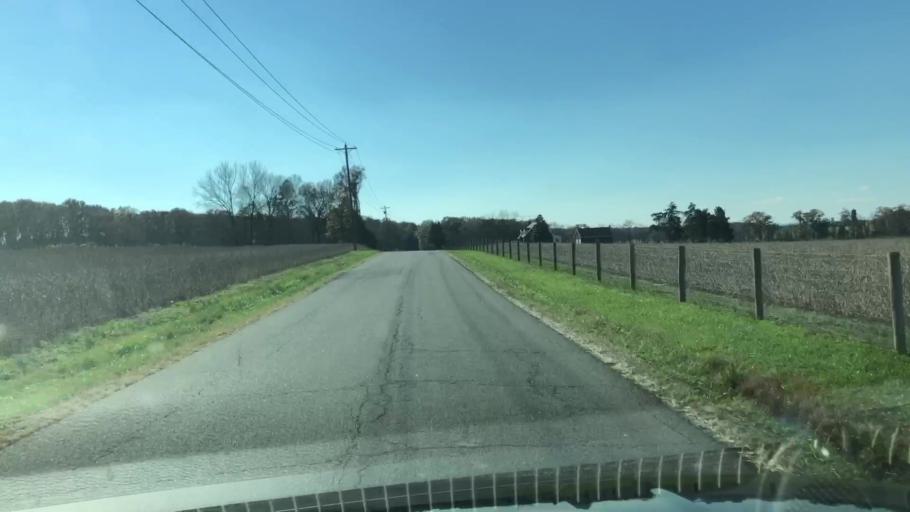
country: US
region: Virginia
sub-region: Fauquier County
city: Bealeton
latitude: 38.5126
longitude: -77.7561
